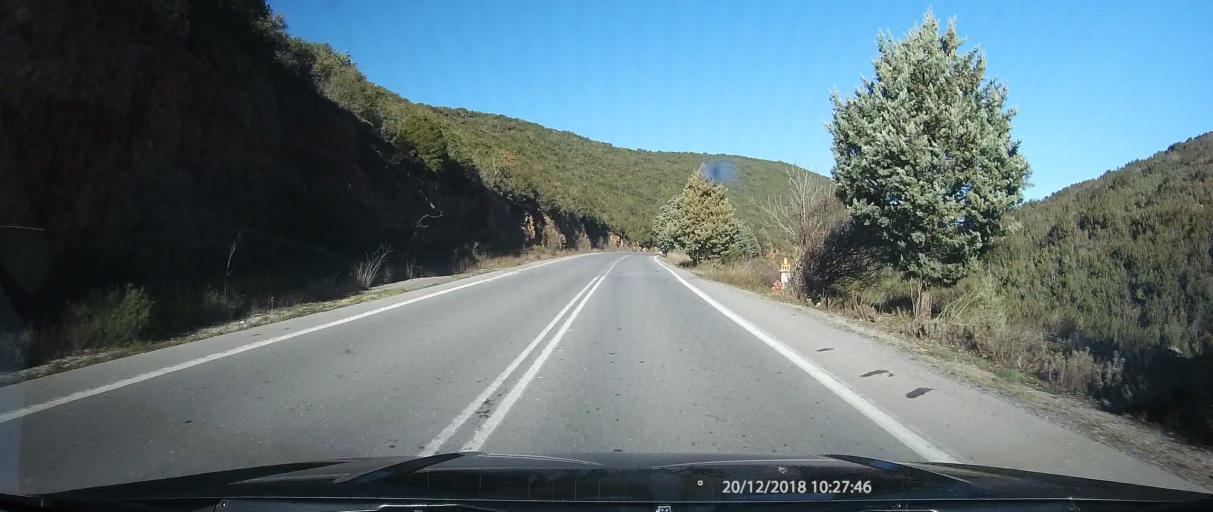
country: GR
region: Peloponnese
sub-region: Nomos Lakonias
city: Kariai
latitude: 37.2503
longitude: 22.4375
